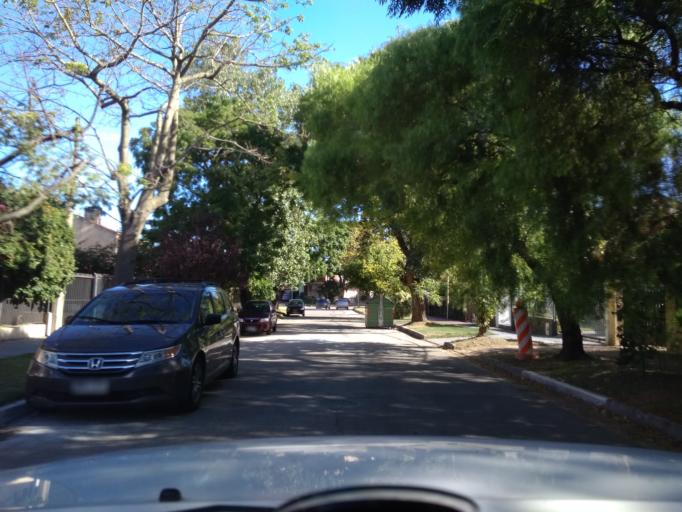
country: UY
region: Canelones
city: Paso de Carrasco
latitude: -34.8919
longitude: -56.0818
